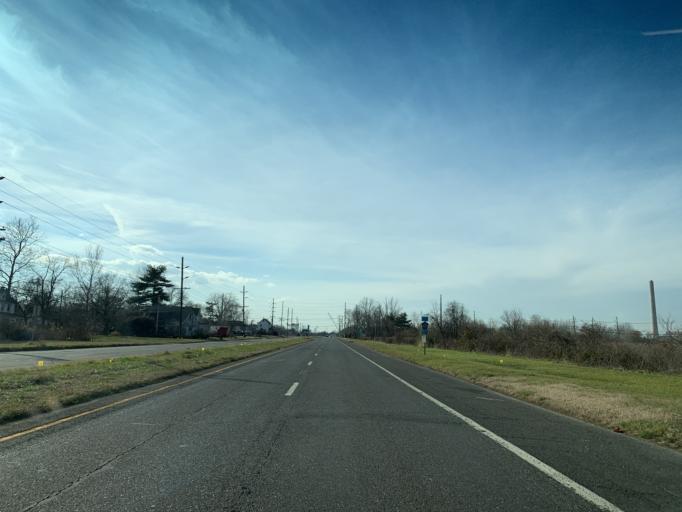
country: US
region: Pennsylvania
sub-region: Delaware County
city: Marcus Hook
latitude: 39.7891
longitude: -75.3935
